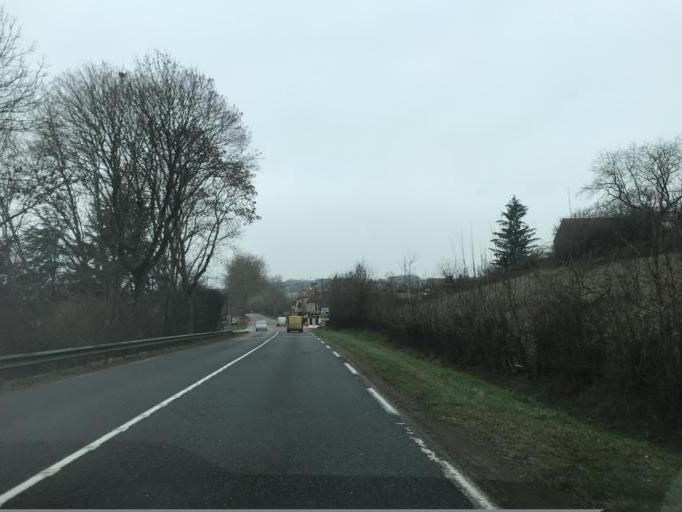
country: FR
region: Bourgogne
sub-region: Departement de l'Yonne
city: Avallon
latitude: 47.5109
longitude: 3.8428
